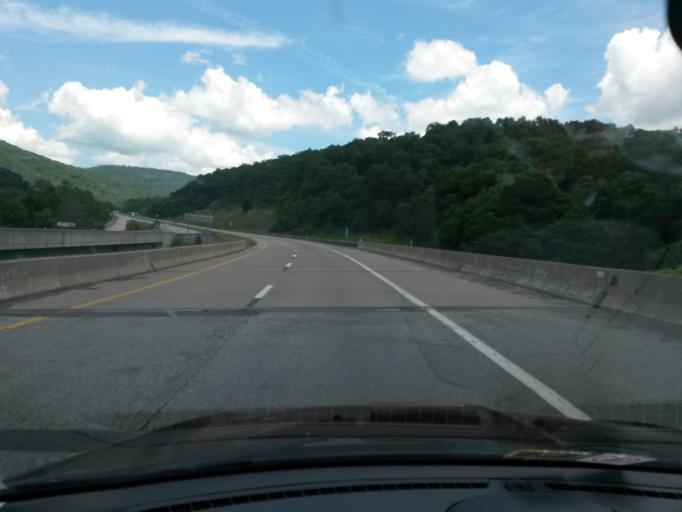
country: US
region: West Virginia
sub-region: Summers County
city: Hinton
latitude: 37.8061
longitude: -80.8163
